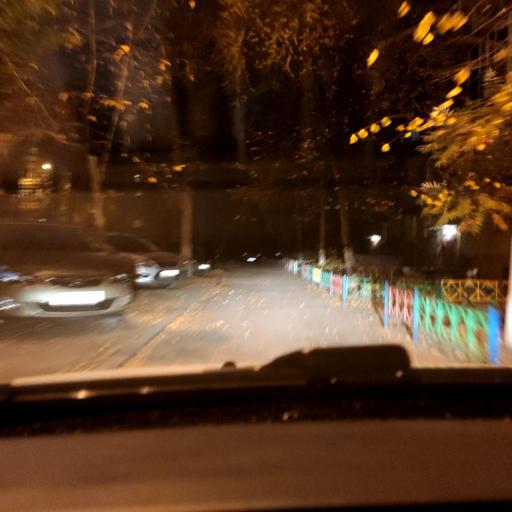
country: RU
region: Voronezj
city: Voronezh
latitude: 51.6474
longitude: 39.1496
